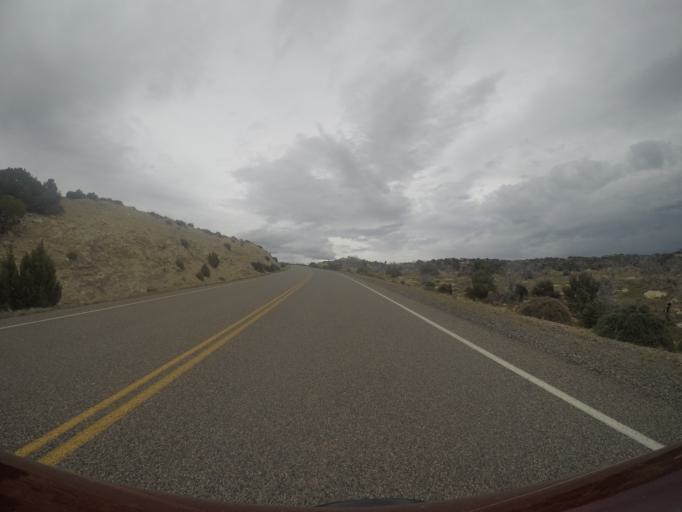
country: US
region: Wyoming
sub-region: Big Horn County
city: Lovell
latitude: 44.9918
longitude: -108.2608
